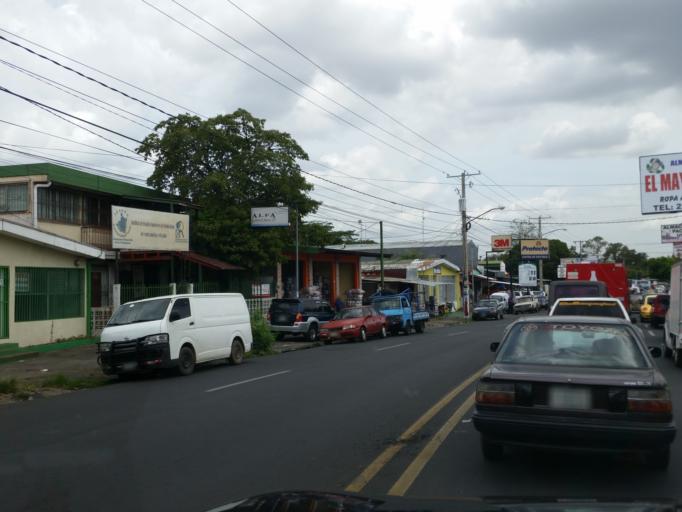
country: NI
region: Managua
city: Managua
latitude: 12.1451
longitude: -86.2519
